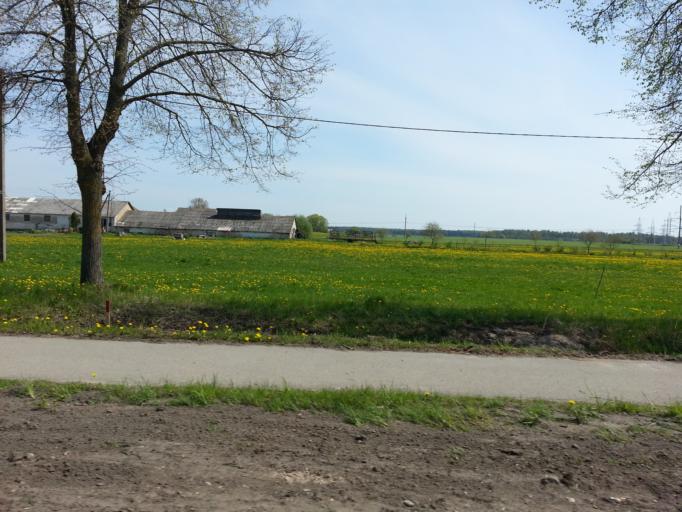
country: LT
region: Panevezys
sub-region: Panevezys City
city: Panevezys
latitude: 55.7657
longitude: 24.2993
